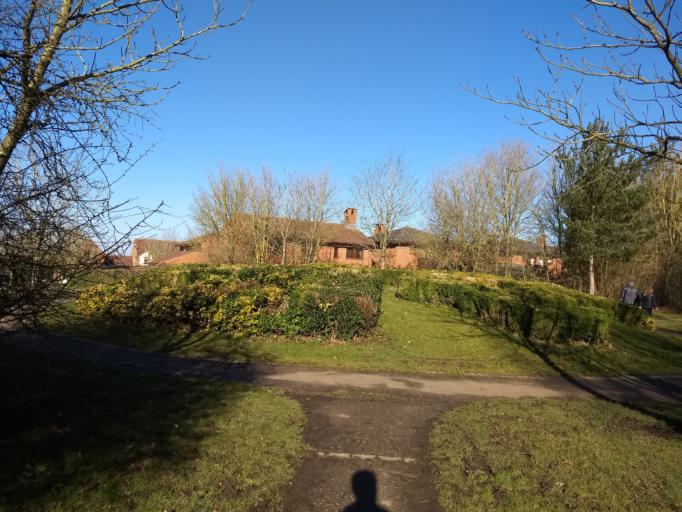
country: GB
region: England
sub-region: Milton Keynes
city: Shenley Church End
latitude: 52.0033
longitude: -0.7848
